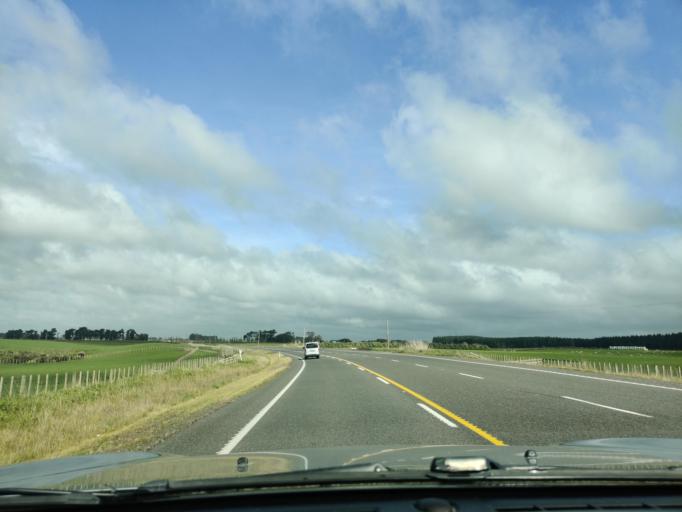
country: NZ
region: Manawatu-Wanganui
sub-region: Rangitikei District
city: Bulls
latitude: -40.0897
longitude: 175.2722
